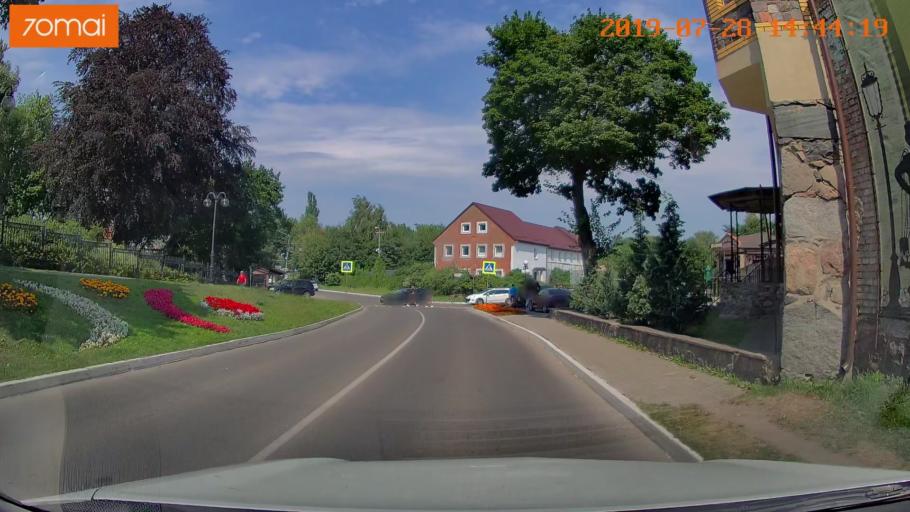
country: RU
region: Kaliningrad
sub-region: Gorod Kaliningrad
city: Yantarnyy
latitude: 54.8667
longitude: 19.9389
